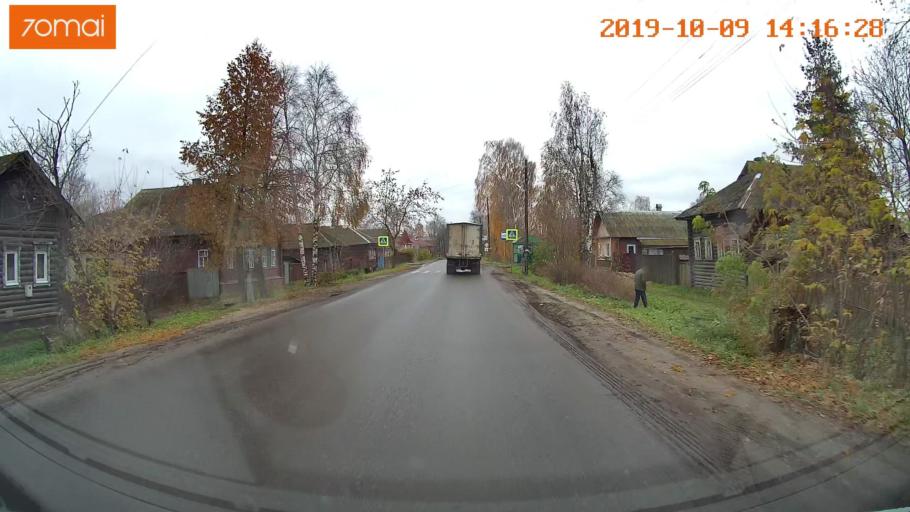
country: RU
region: Kostroma
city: Buy
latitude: 58.4820
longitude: 41.5191
